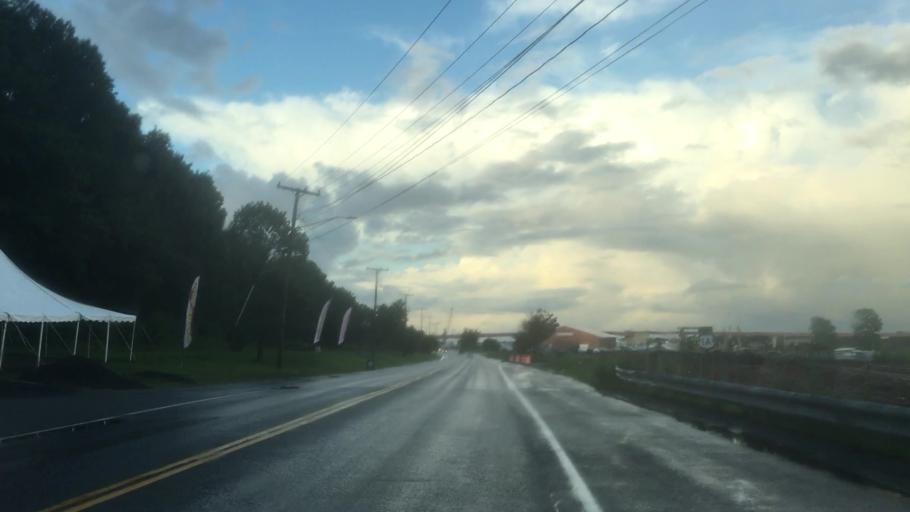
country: US
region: Maine
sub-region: Cumberland County
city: Portland
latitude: 43.6432
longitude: -70.2722
